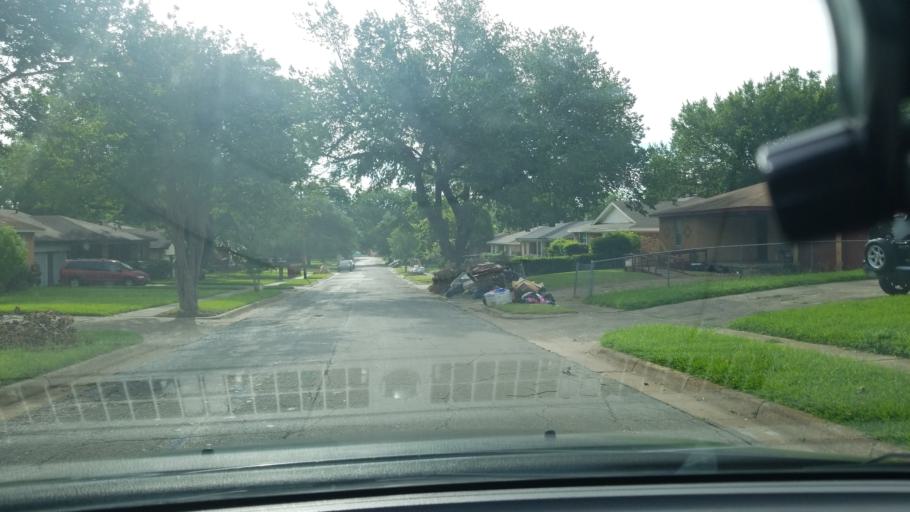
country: US
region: Texas
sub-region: Dallas County
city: Balch Springs
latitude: 32.7553
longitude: -96.6709
